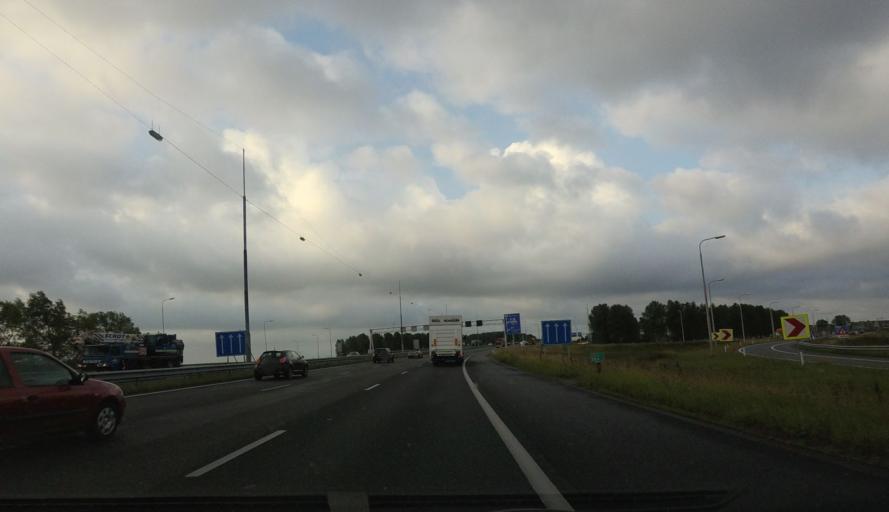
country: NL
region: North Holland
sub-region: Gemeente Uitgeest
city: Uitgeest
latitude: 52.5189
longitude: 4.7181
